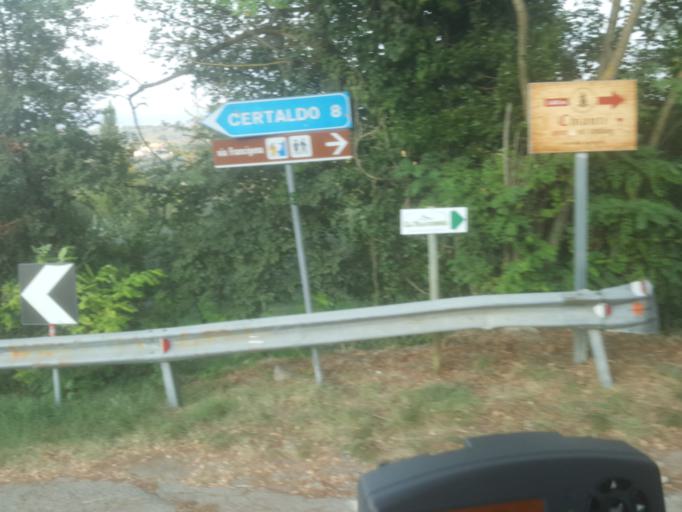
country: IT
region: Tuscany
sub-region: Province of Florence
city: Gambassi Terme
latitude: 43.5395
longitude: 10.9626
